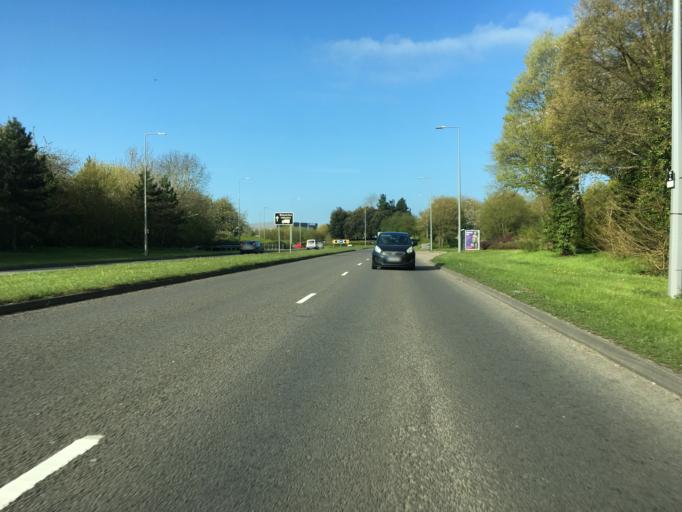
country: GB
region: England
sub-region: Milton Keynes
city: Milton Keynes
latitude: 52.0621
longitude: -0.7558
